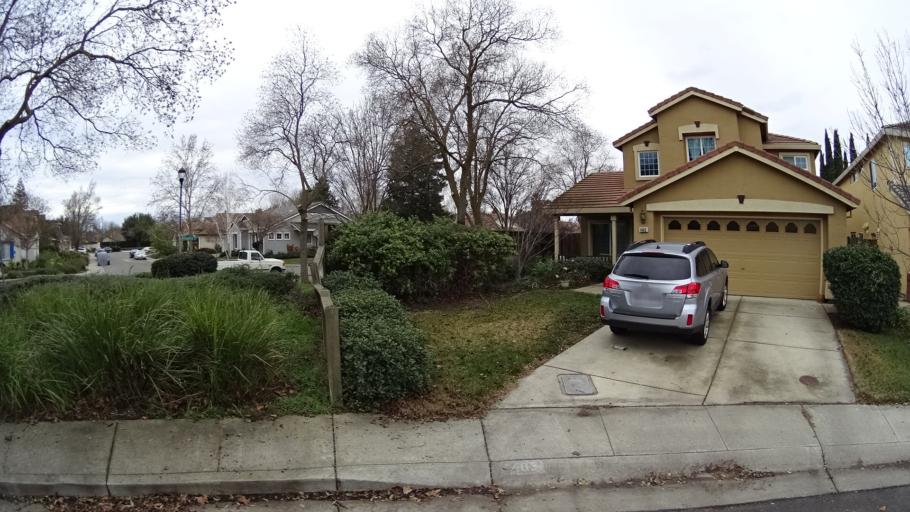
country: US
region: California
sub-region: Yolo County
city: Davis
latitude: 38.5593
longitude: -121.7001
